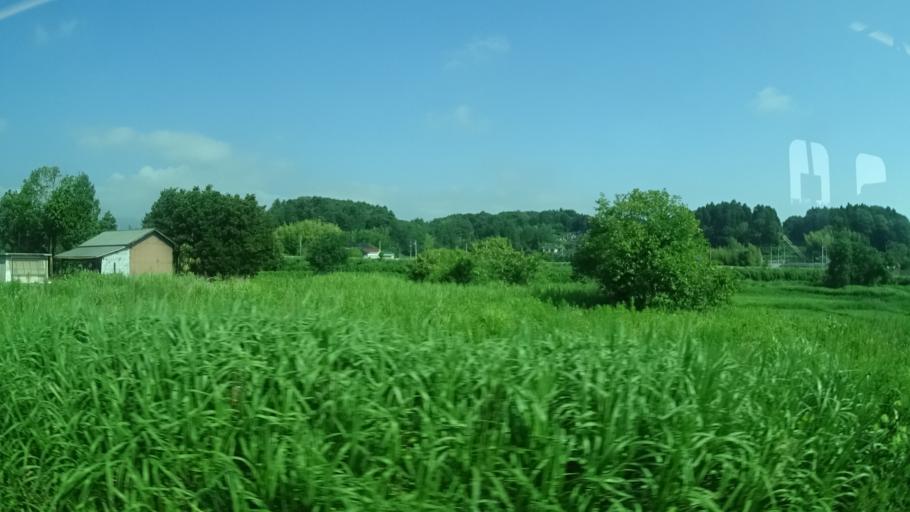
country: JP
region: Fukushima
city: Namie
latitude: 37.3203
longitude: 141.0107
